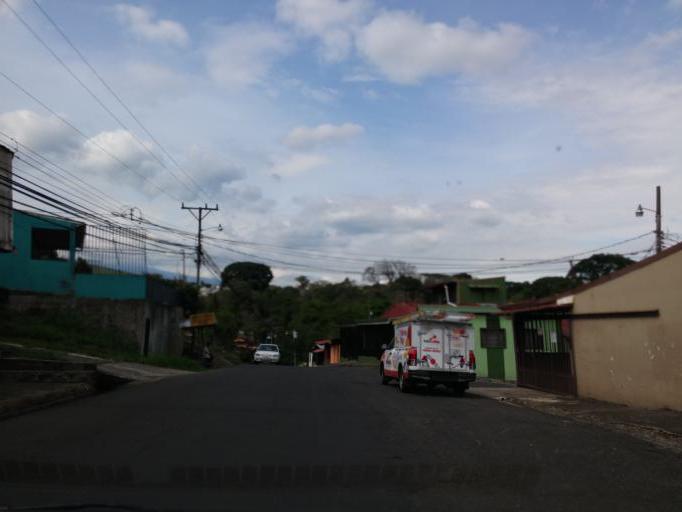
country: CR
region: Alajuela
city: Alajuela
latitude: 10.0079
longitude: -84.2016
